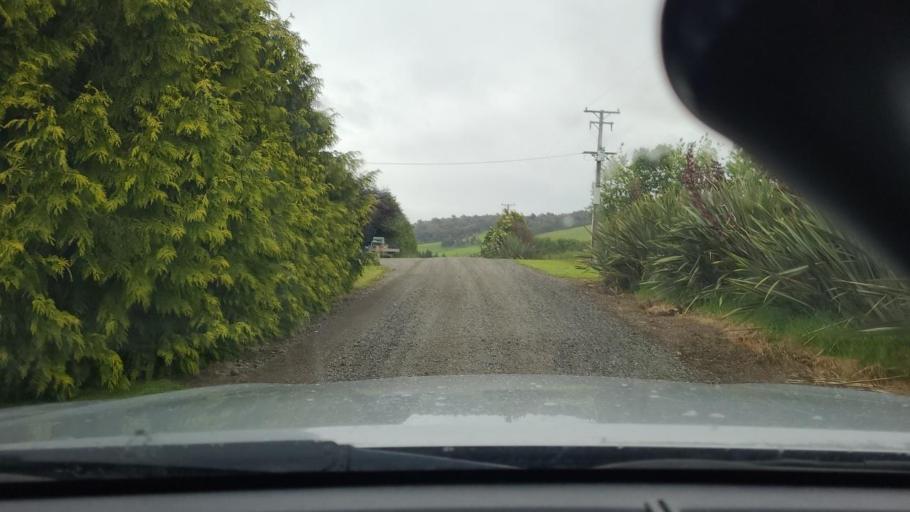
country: NZ
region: Southland
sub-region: Southland District
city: Riverton
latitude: -46.1916
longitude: 168.0213
